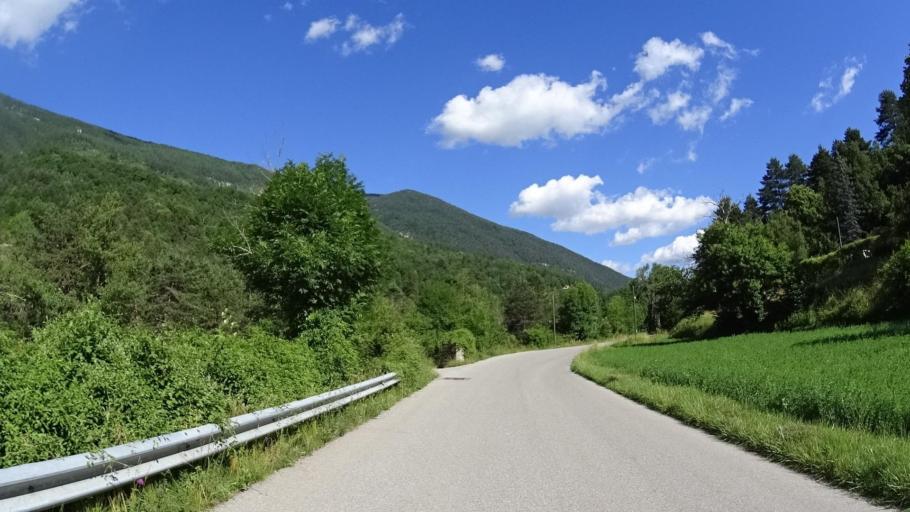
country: FR
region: Provence-Alpes-Cote d'Azur
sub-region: Departement des Alpes-de-Haute-Provence
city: Annot
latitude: 43.9742
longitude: 6.6544
